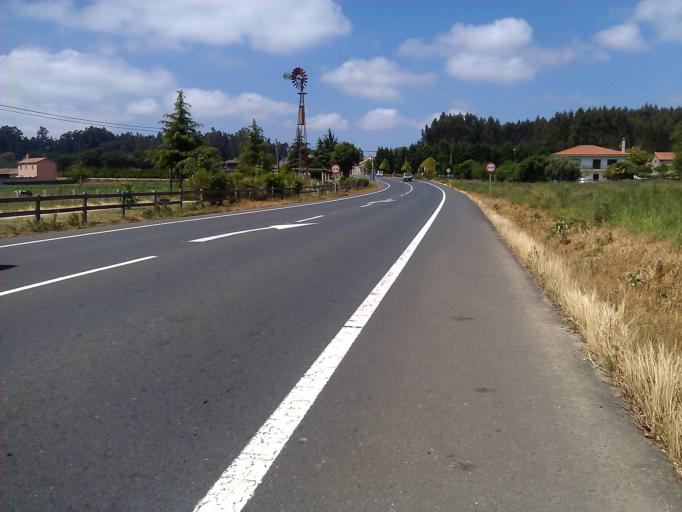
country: ES
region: Galicia
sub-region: Provincia da Coruna
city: Touro
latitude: 42.9169
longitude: -8.3160
